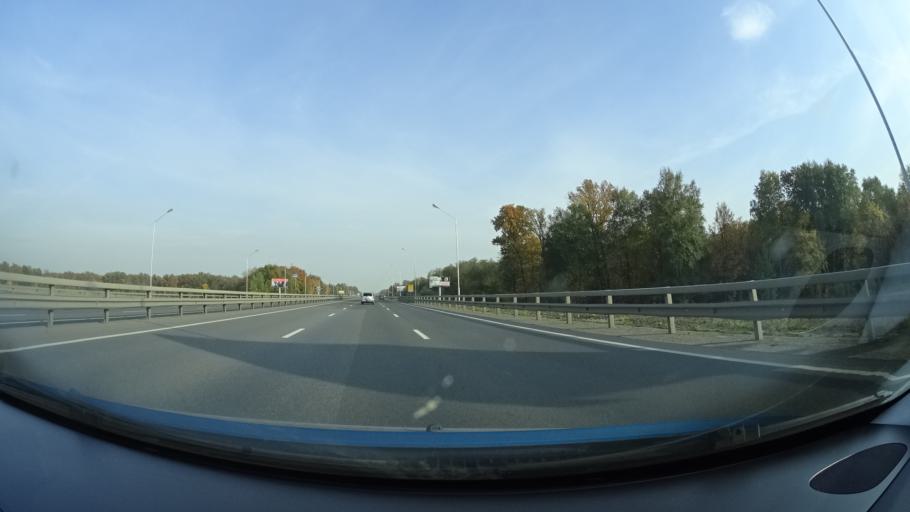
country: RU
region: Bashkortostan
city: Avdon
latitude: 54.6675
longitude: 55.8497
